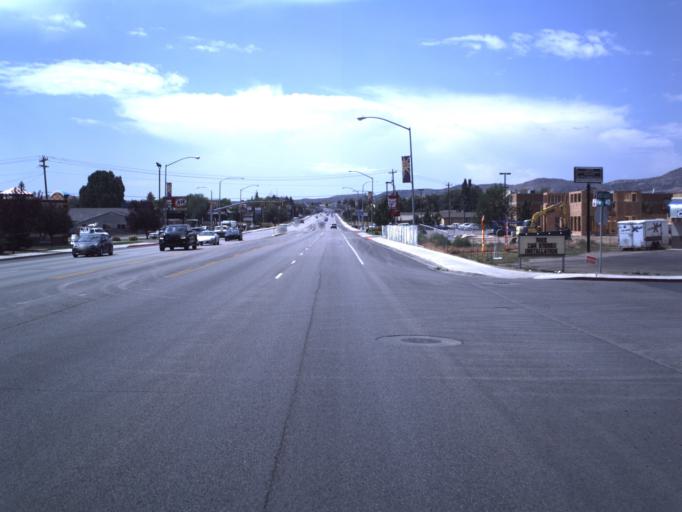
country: US
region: Utah
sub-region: Uintah County
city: Vernal
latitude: 40.4495
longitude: -109.5517
